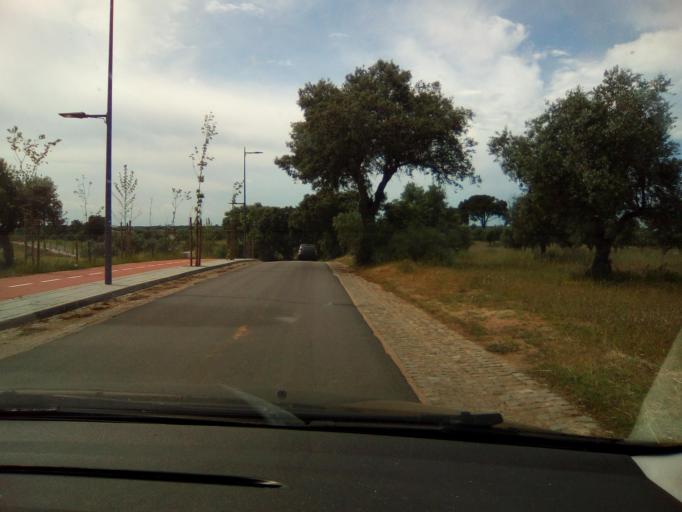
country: PT
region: Portalegre
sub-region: Avis
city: Avis
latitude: 39.0545
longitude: -7.9038
